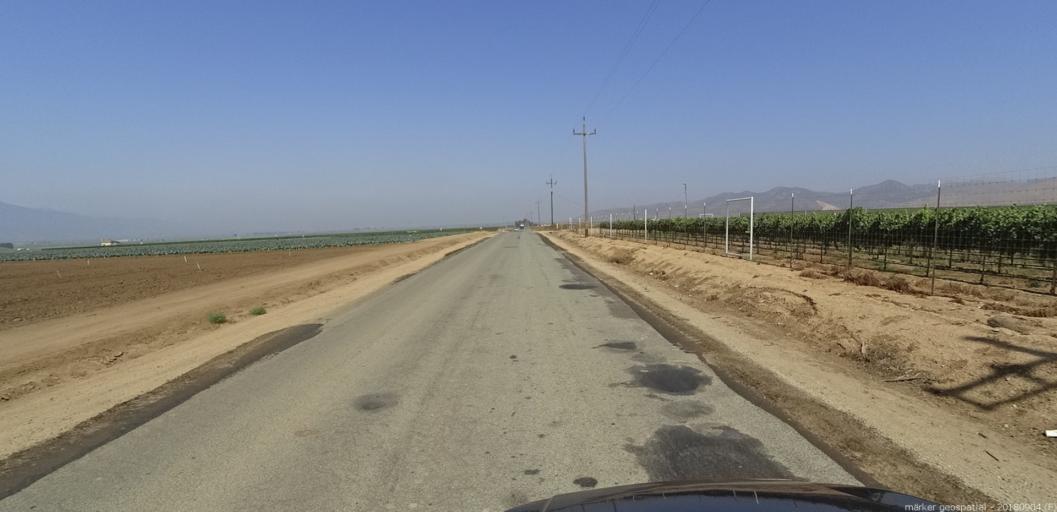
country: US
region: California
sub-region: Monterey County
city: Gonzales
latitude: 36.5275
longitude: -121.4181
